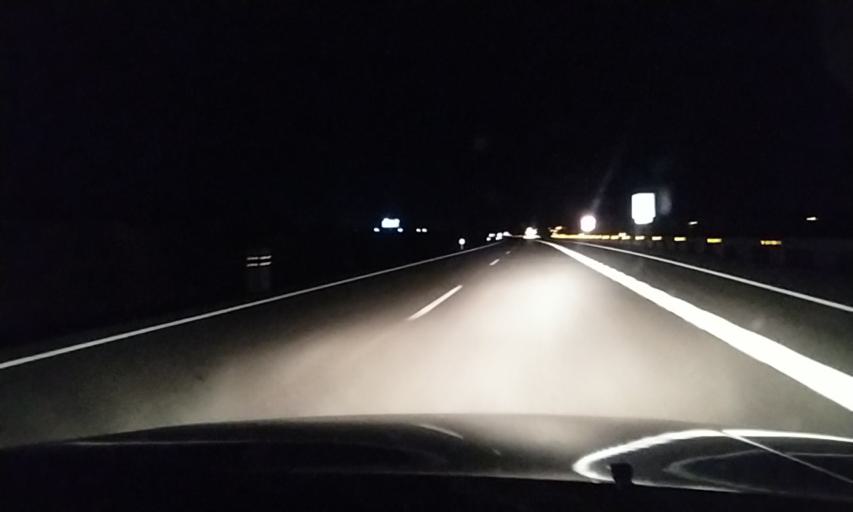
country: ES
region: Castille and Leon
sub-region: Provincia de Leon
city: La Baneza
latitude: 42.2901
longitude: -5.9210
